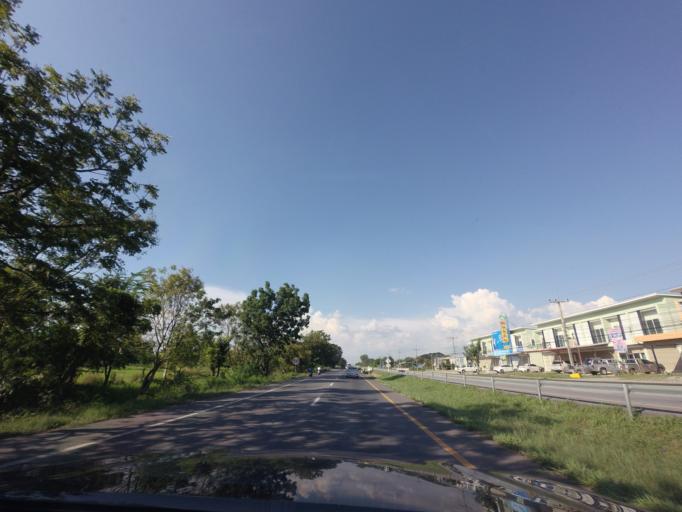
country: TH
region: Khon Kaen
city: Non Sila
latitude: 15.9700
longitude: 102.6925
